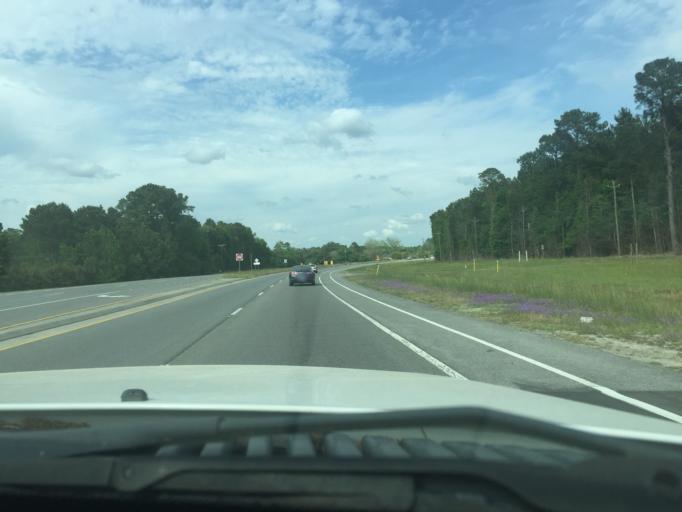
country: US
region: Georgia
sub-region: Chatham County
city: Georgetown
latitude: 31.9930
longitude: -81.2743
